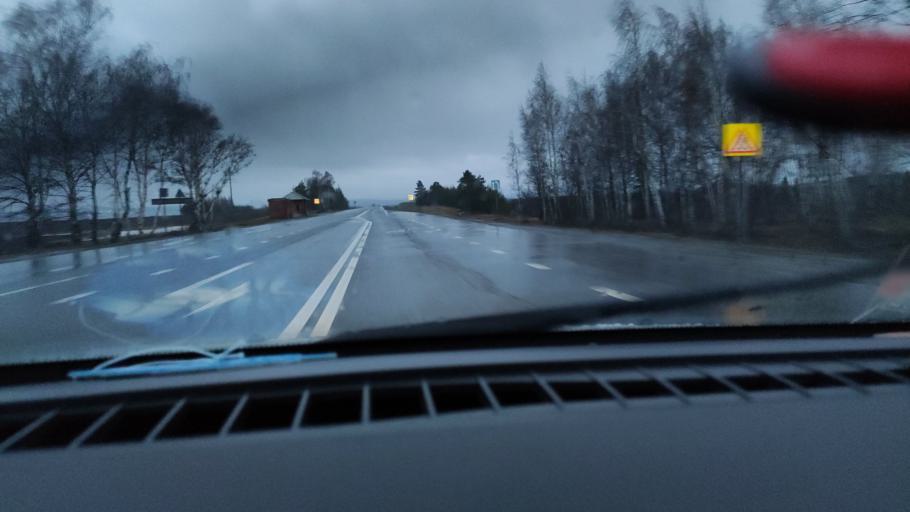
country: RU
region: Udmurtiya
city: Alnashi
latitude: 56.2156
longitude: 52.4285
